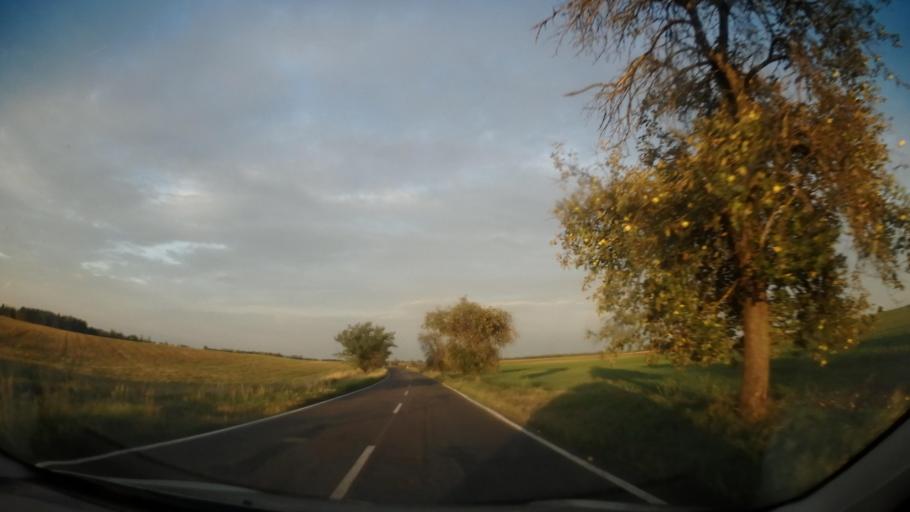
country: CZ
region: Central Bohemia
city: Milovice
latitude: 50.2254
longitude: 14.9078
